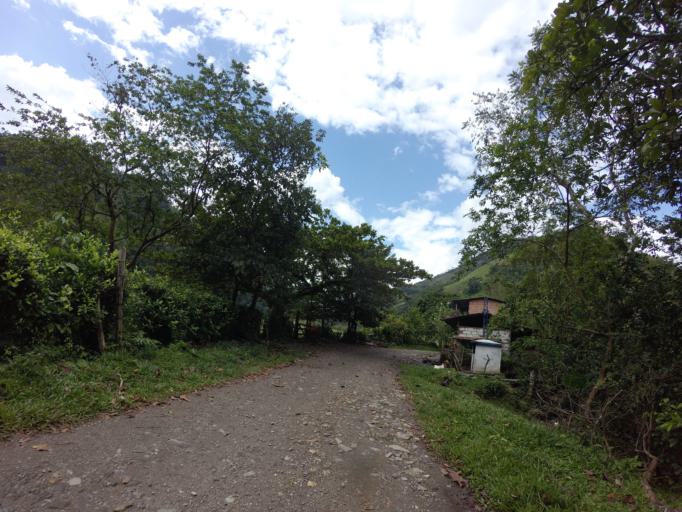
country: CO
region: Antioquia
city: Narino
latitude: 5.5320
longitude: -75.1501
